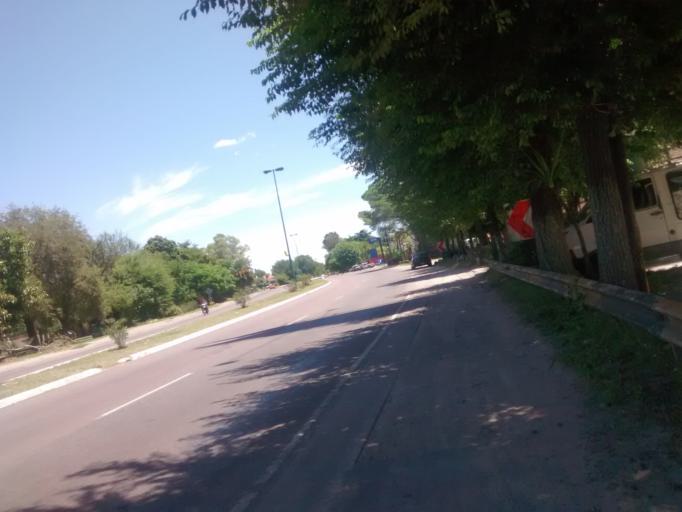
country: AR
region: Buenos Aires
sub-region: Partido de La Plata
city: La Plata
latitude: -34.8637
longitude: -58.0470
